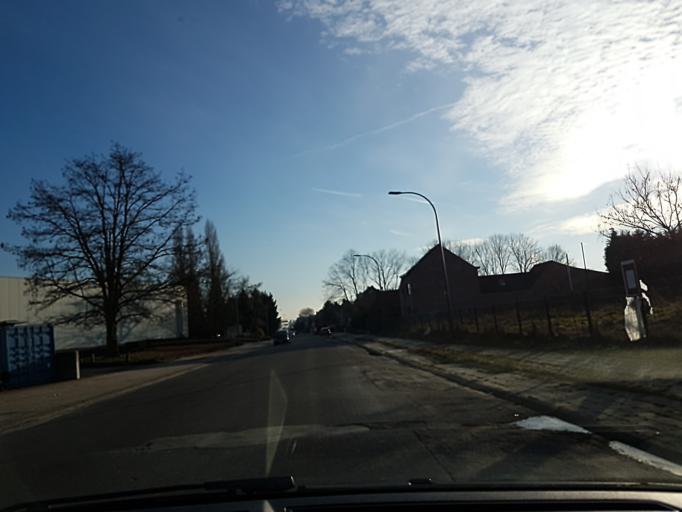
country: BE
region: Flanders
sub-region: Provincie Antwerpen
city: Aartselaar
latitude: 51.1601
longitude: 4.3807
